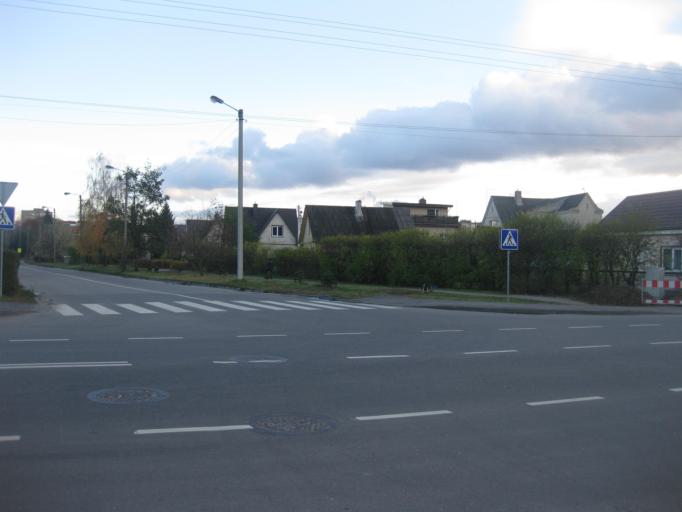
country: LT
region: Kauno apskritis
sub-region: Kaunas
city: Silainiai
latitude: 54.9198
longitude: 23.8981
